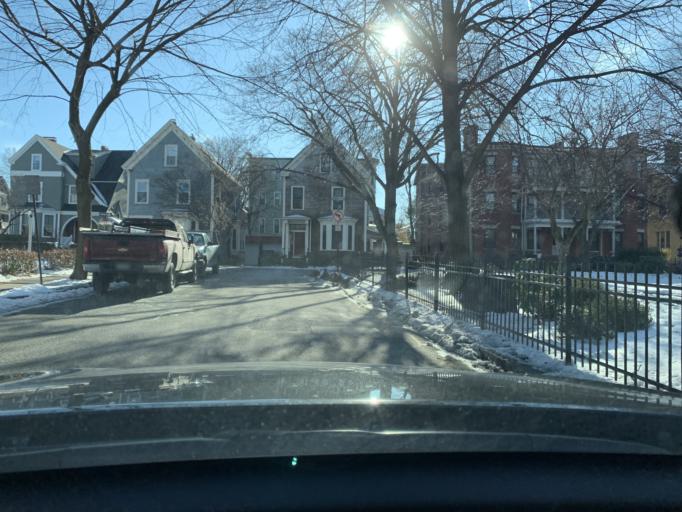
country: US
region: Massachusetts
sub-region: Norfolk County
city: Brookline
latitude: 42.3355
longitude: -71.1168
